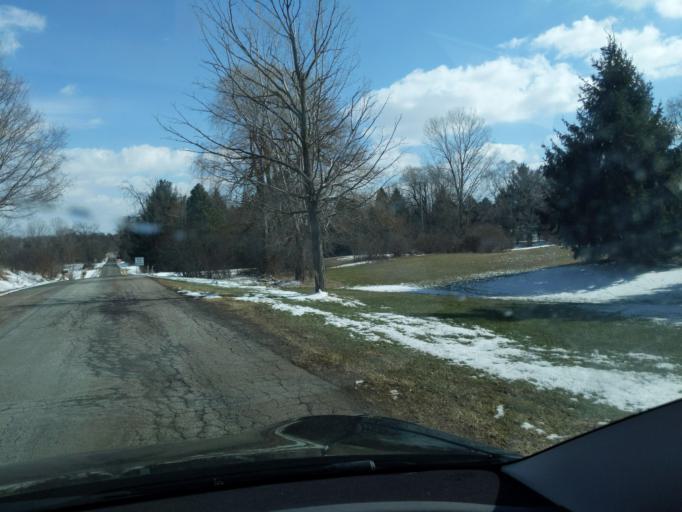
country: US
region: Michigan
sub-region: Ingham County
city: Williamston
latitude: 42.6155
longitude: -84.2756
